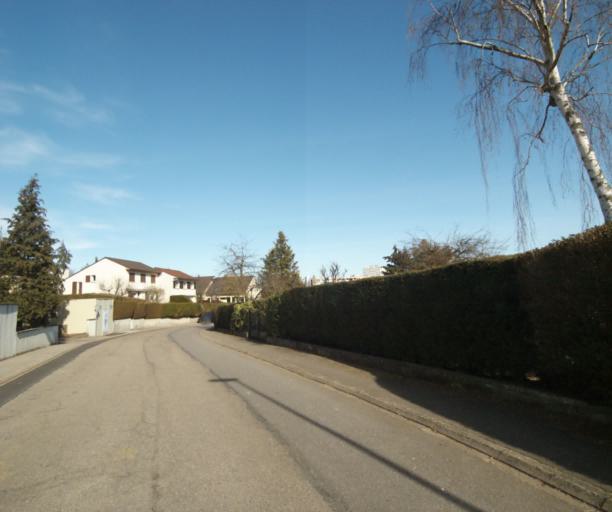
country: FR
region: Lorraine
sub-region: Departement de Meurthe-et-Moselle
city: Laxou
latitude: 48.6756
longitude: 6.1414
